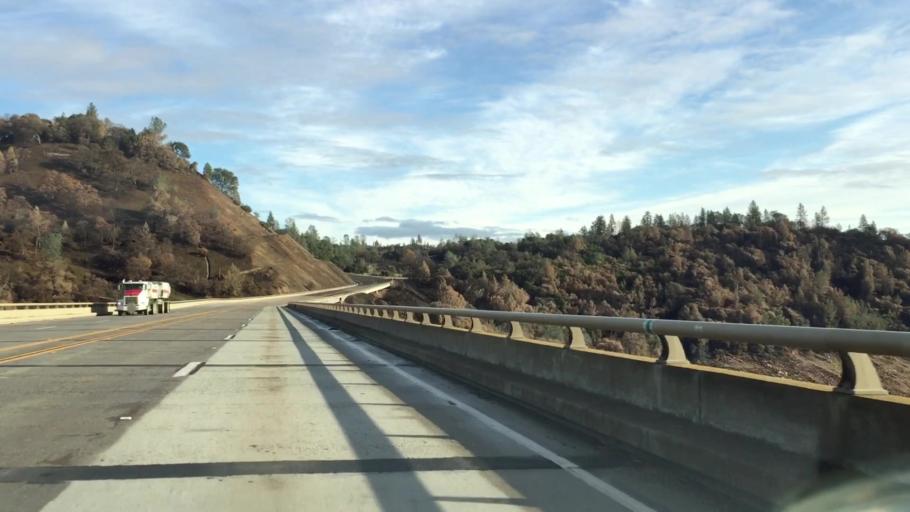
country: US
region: California
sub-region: Butte County
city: Berry Creek
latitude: 39.6656
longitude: -121.5315
